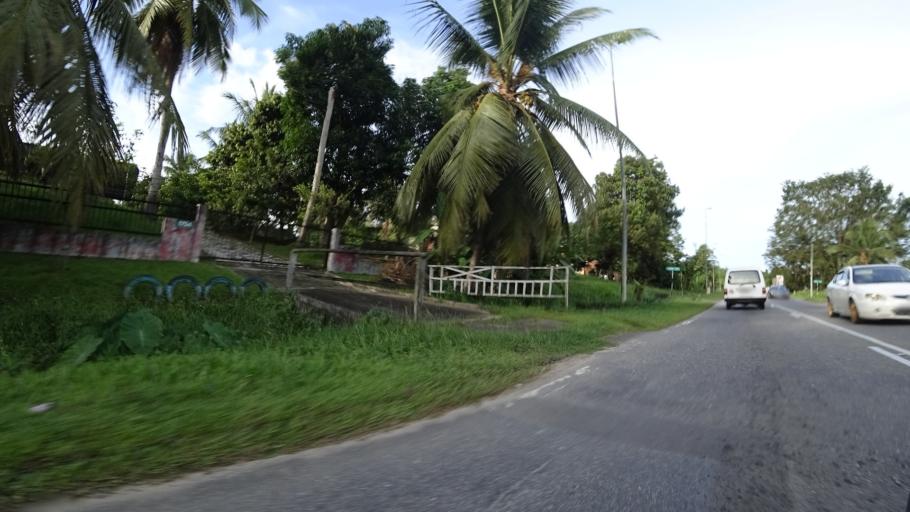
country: BN
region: Brunei and Muara
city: Bandar Seri Begawan
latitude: 4.8740
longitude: 114.8263
